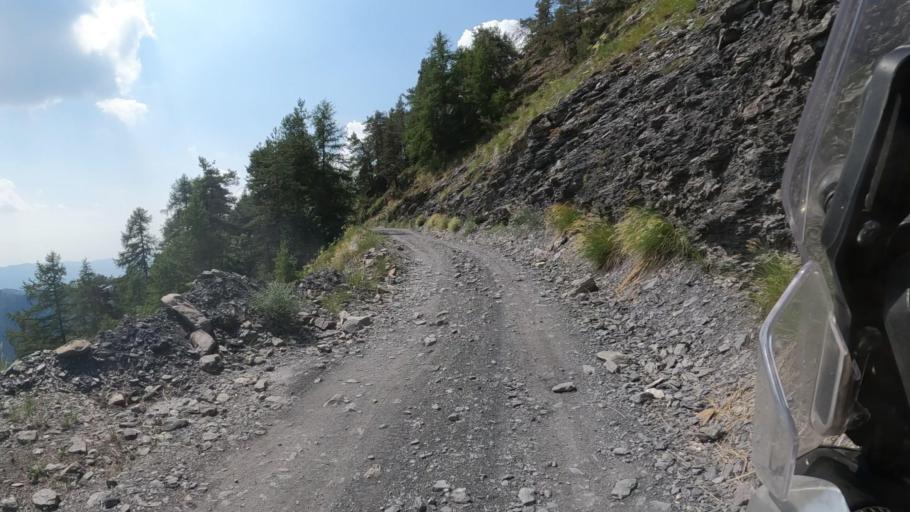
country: IT
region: Piedmont
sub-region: Provincia di Cuneo
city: Briga Alta
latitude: 44.0407
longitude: 7.7012
